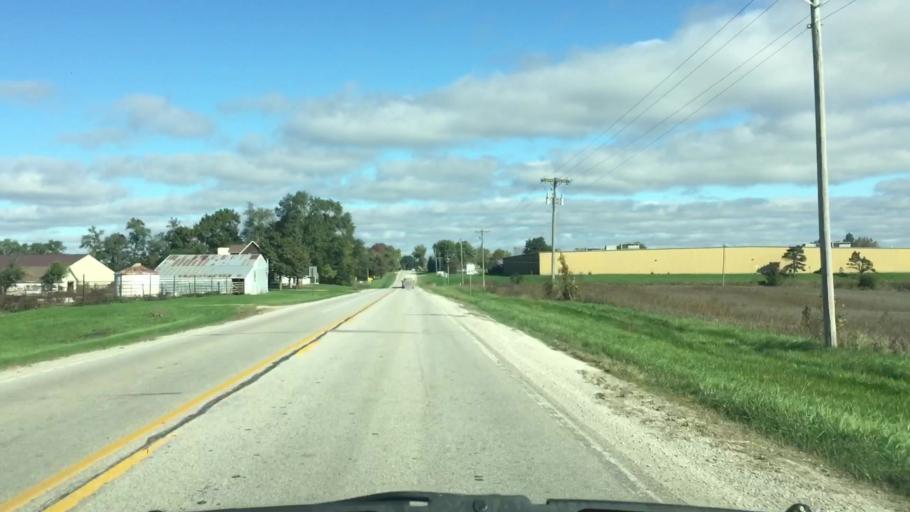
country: US
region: Iowa
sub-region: Decatur County
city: Leon
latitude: 40.7304
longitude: -93.7612
